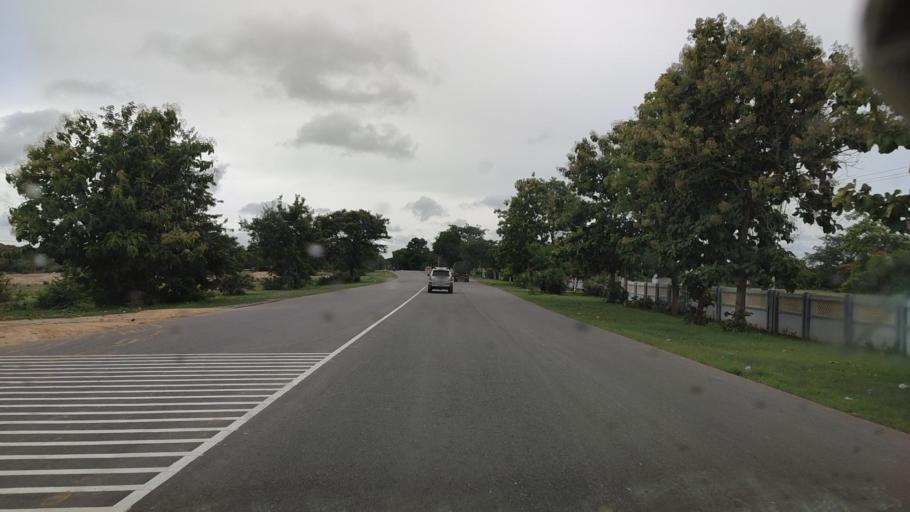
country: MM
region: Mandalay
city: Meiktila
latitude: 20.8365
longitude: 95.8953
